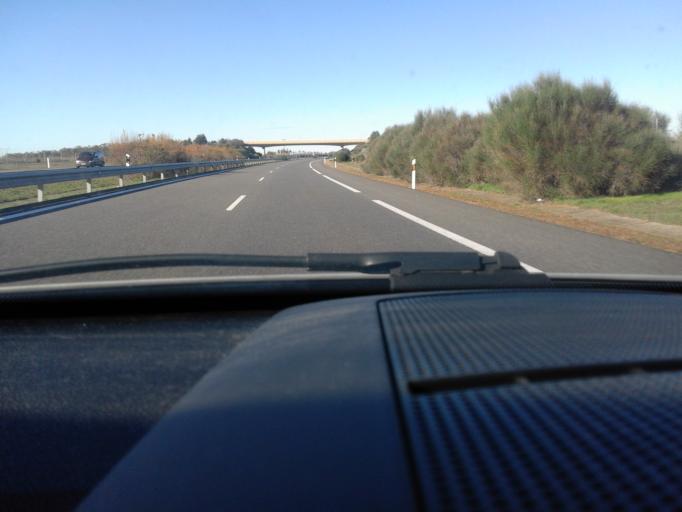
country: ES
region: Castille and Leon
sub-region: Provincia de Leon
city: Villamoratiel de las Matas
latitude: 42.4207
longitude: -5.2798
